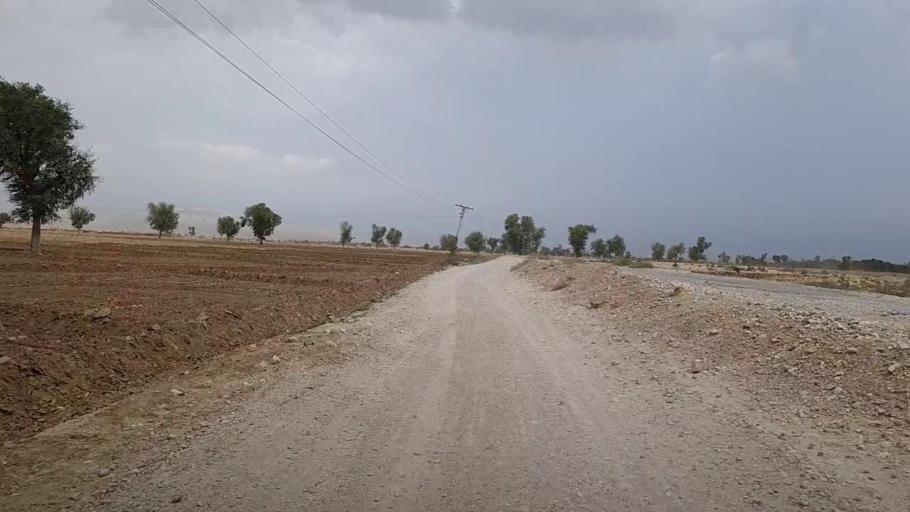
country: PK
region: Sindh
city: Sehwan
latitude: 26.3107
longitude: 67.7304
